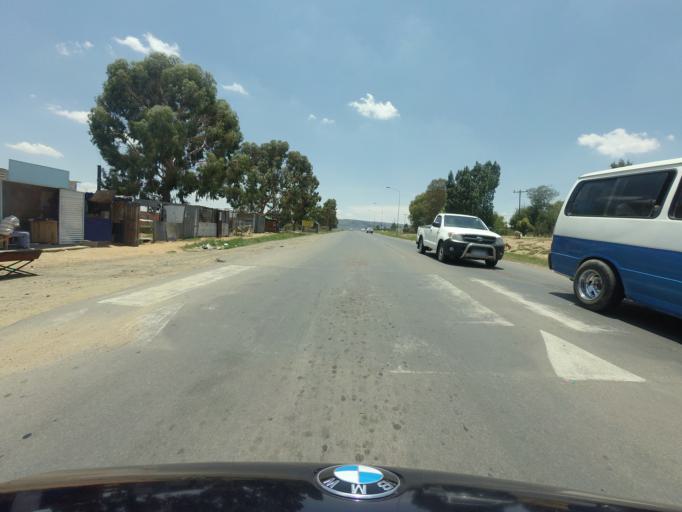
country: LS
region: Maseru
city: Maseru
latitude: -29.2690
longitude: 27.5373
